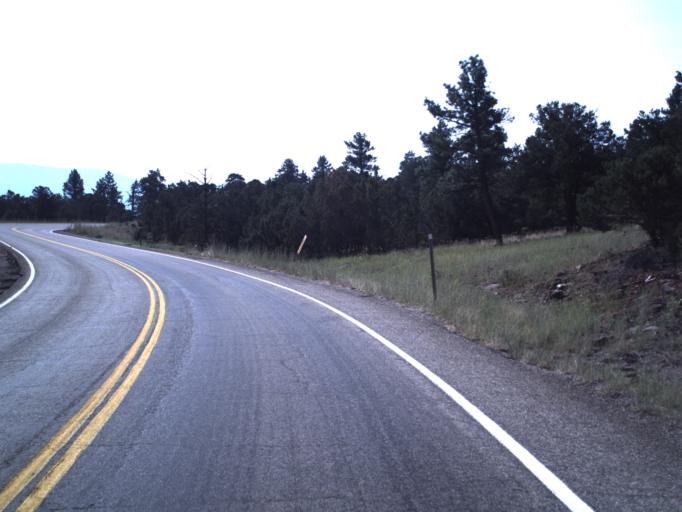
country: US
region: Utah
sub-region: Daggett County
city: Manila
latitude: 40.8959
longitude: -109.4465
